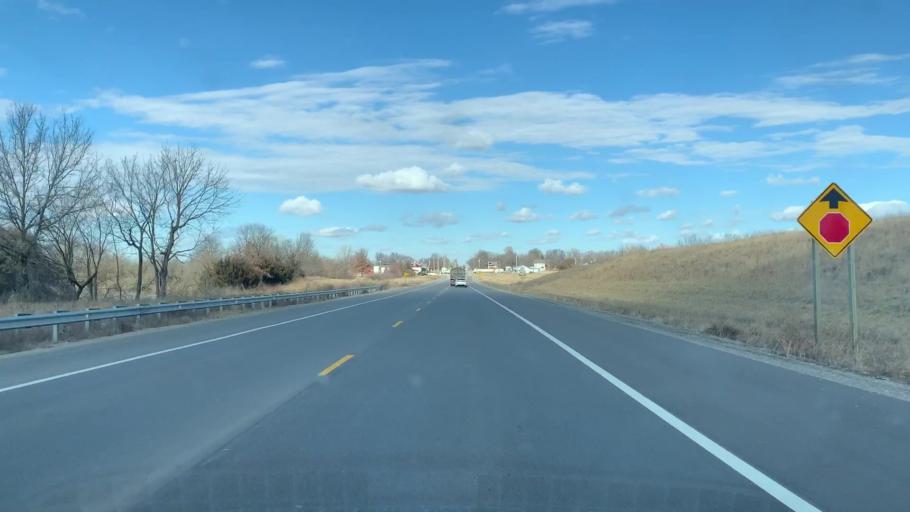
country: US
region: Kansas
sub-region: Crawford County
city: Pittsburg
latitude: 37.3352
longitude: -94.8321
